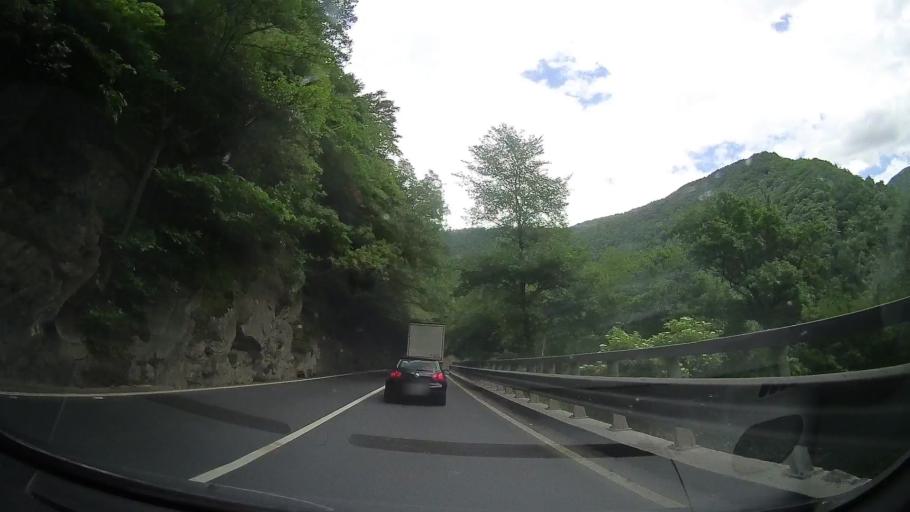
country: RO
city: Cainenii Mici
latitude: 45.5543
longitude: 24.2640
